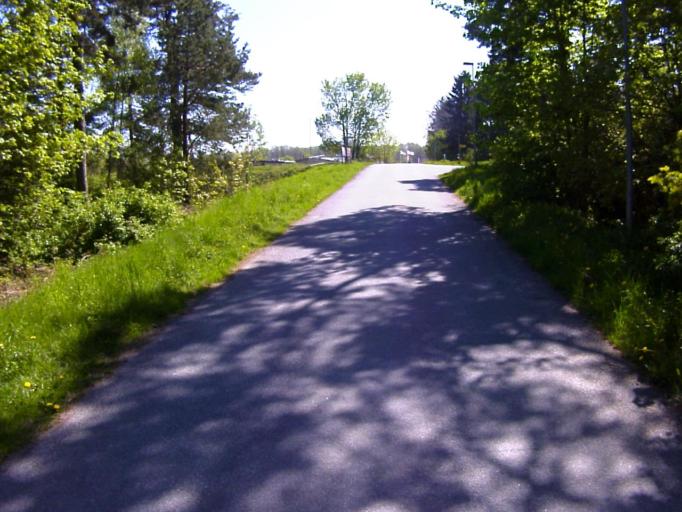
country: SE
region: Skane
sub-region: Kristianstads Kommun
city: Degeberga
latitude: 55.9005
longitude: 14.0964
